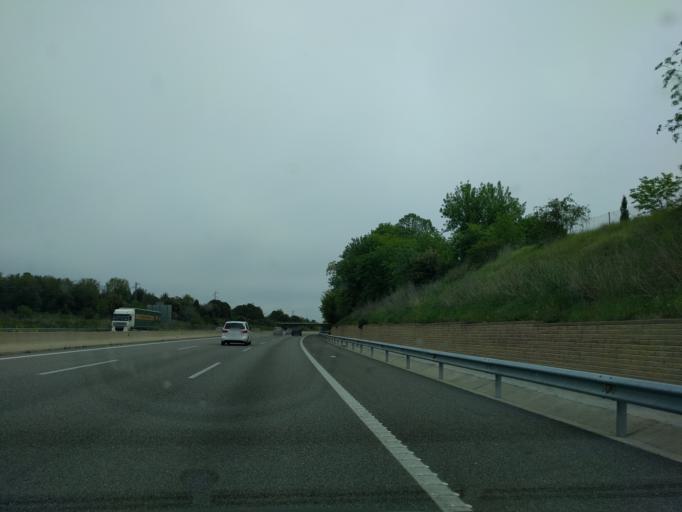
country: ES
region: Catalonia
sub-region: Provincia de Girona
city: Aiguaviva
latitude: 41.9184
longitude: 2.7750
